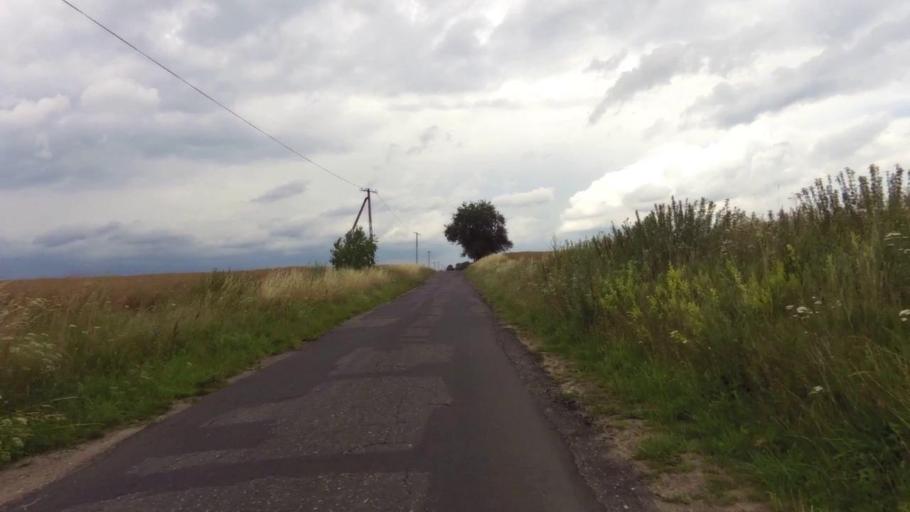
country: PL
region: West Pomeranian Voivodeship
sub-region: Powiat gryfinski
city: Moryn
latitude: 52.8902
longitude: 14.4069
